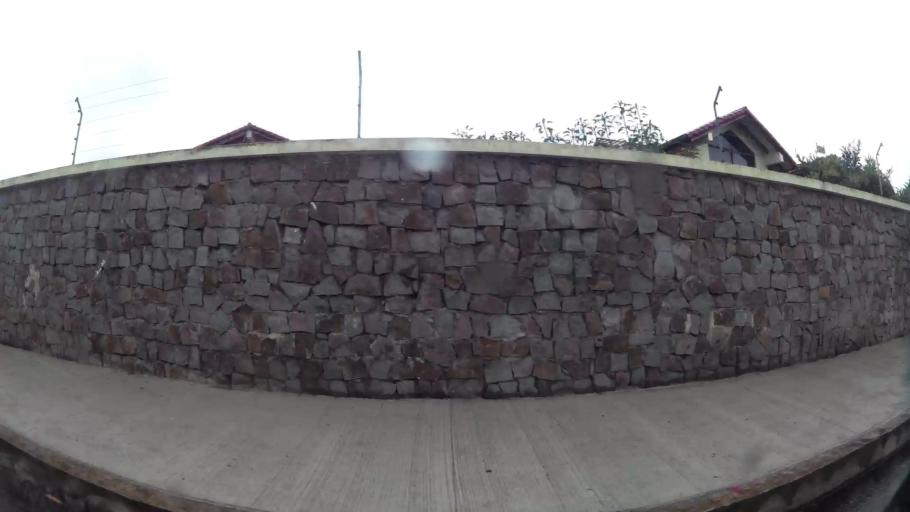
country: EC
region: Pichincha
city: Sangolqui
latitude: -0.3014
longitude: -78.4498
